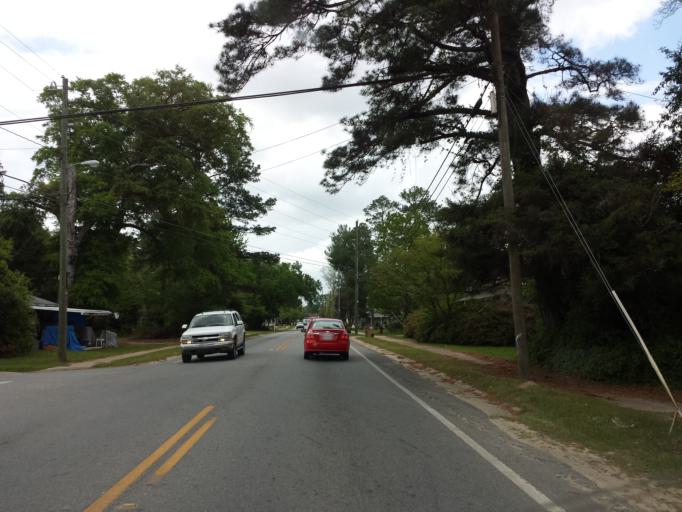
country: US
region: Georgia
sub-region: Cook County
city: Sparks
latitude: 31.1610
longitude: -83.4368
